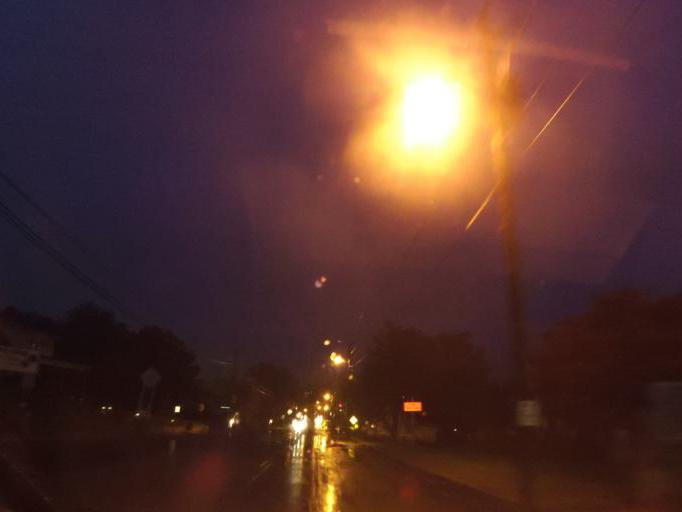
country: US
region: North Carolina
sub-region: Alleghany County
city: Sparta
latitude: 36.5033
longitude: -81.1183
